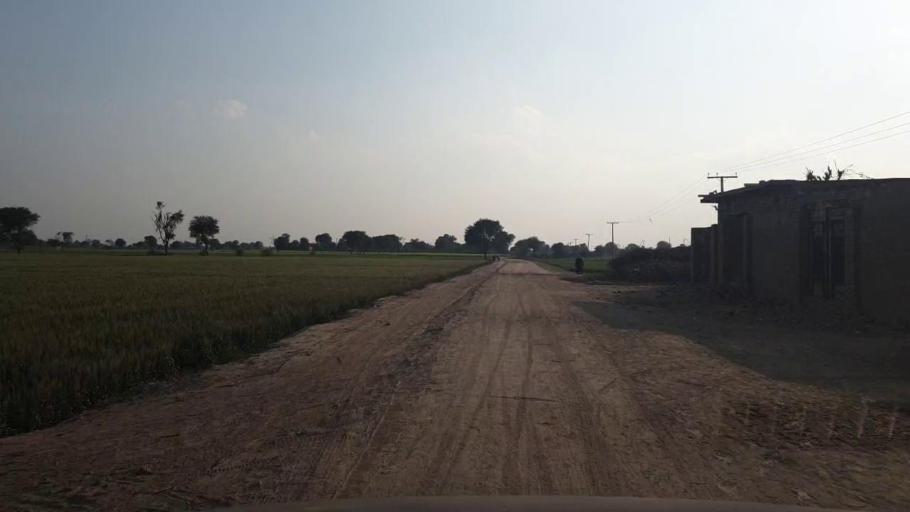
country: PK
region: Sindh
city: Bhit Shah
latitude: 25.7768
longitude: 68.4672
